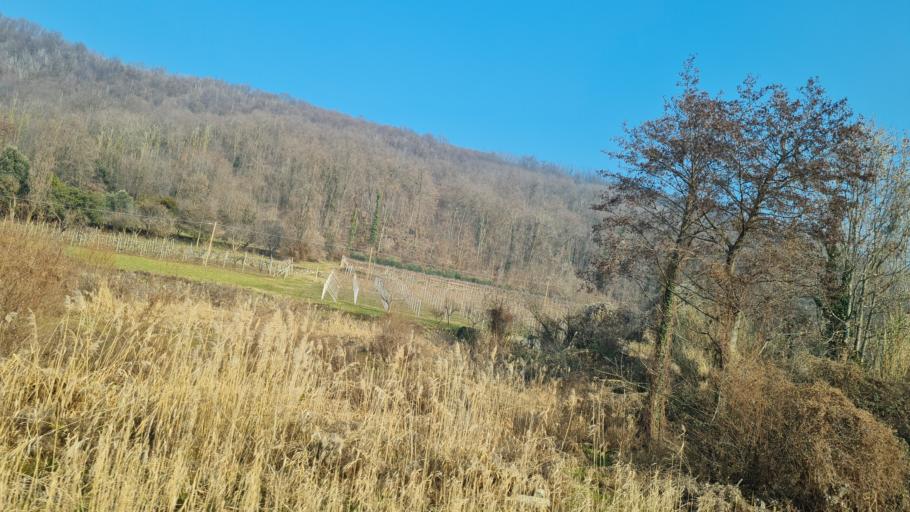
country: IT
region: Piedmont
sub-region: Provincia di Torino
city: Piverone
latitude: 45.4472
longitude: 8.0170
